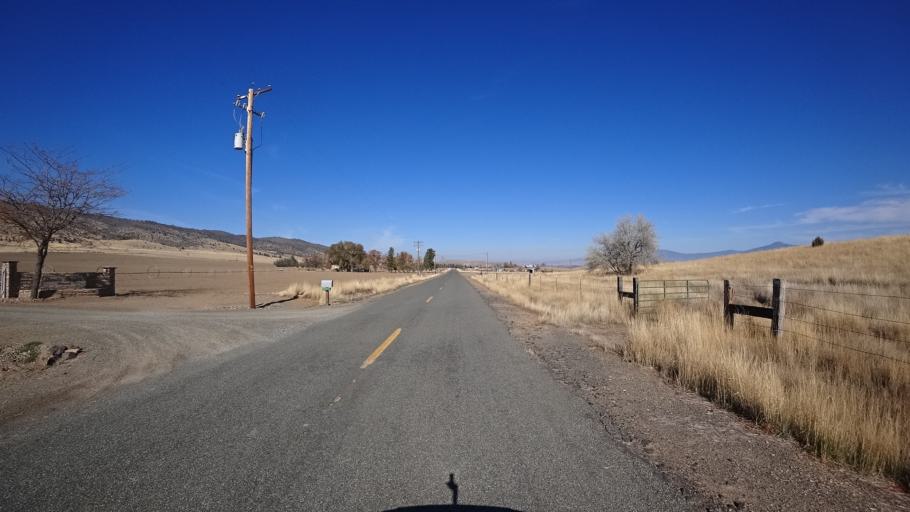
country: US
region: California
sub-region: Siskiyou County
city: Montague
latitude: 41.5725
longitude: -122.5487
